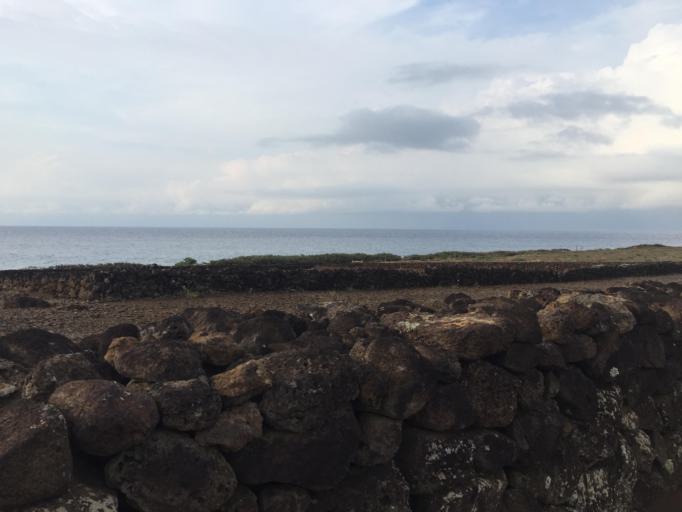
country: US
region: Hawaii
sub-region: Hawaii County
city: Hawi
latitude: 20.2553
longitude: -155.8827
